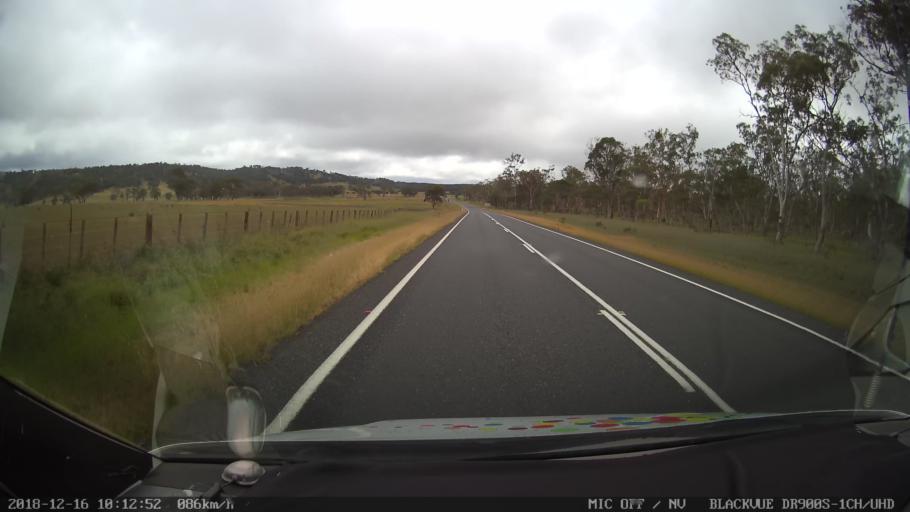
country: AU
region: New South Wales
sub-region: Glen Innes Severn
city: Glen Innes
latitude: -29.3025
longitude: 151.9458
